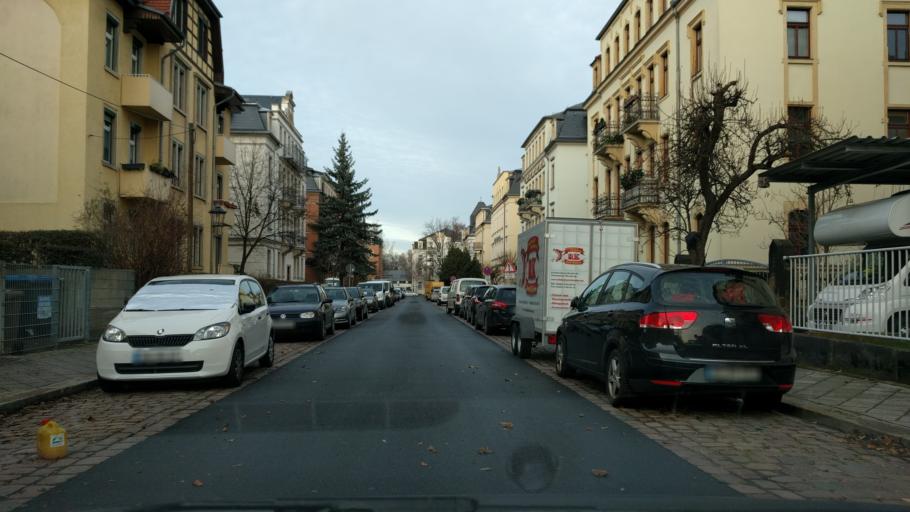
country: DE
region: Saxony
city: Dresden
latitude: 51.0365
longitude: 13.6985
